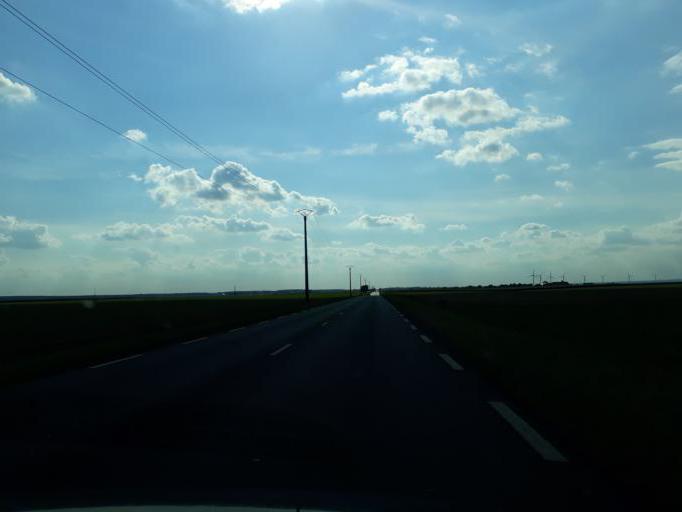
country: FR
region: Centre
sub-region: Departement du Loir-et-Cher
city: Ouzouer-le-Marche
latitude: 47.9042
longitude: 1.4310
